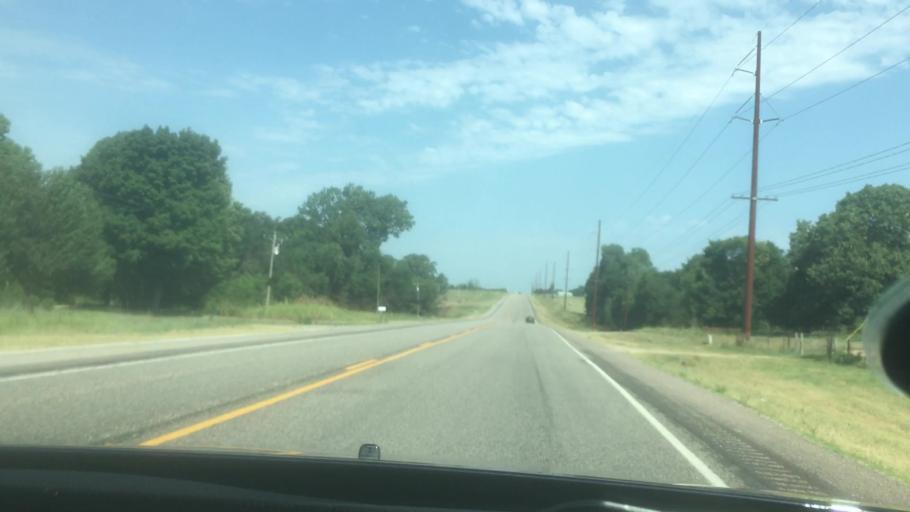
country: US
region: Oklahoma
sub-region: Seminole County
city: Konawa
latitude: 34.8454
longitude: -96.8034
